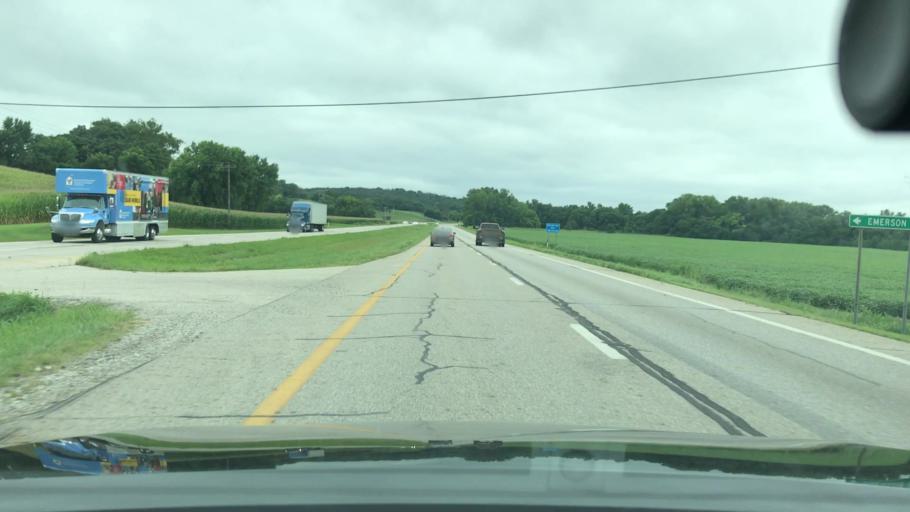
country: US
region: Ohio
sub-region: Pickaway County
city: Logan Elm Village
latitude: 39.5307
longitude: -82.9675
